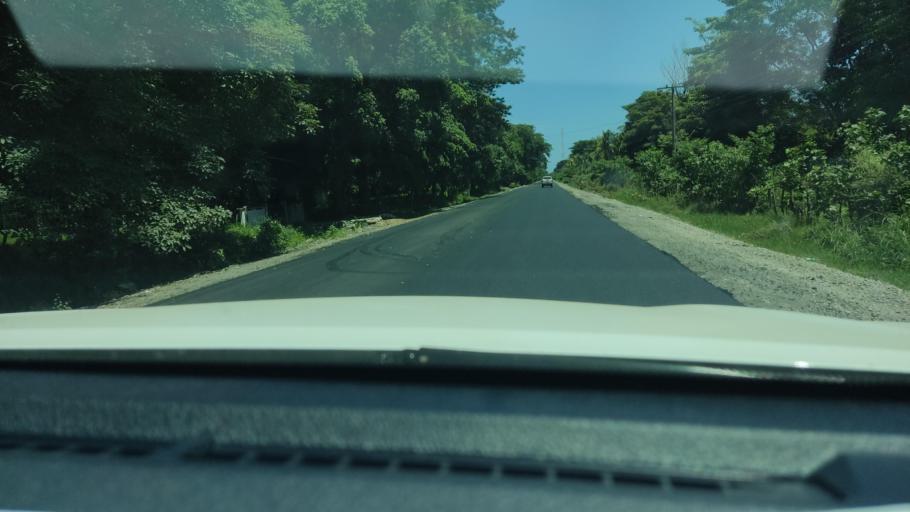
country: SV
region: Ahuachapan
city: San Francisco Menendez
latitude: 13.8351
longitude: -90.1197
